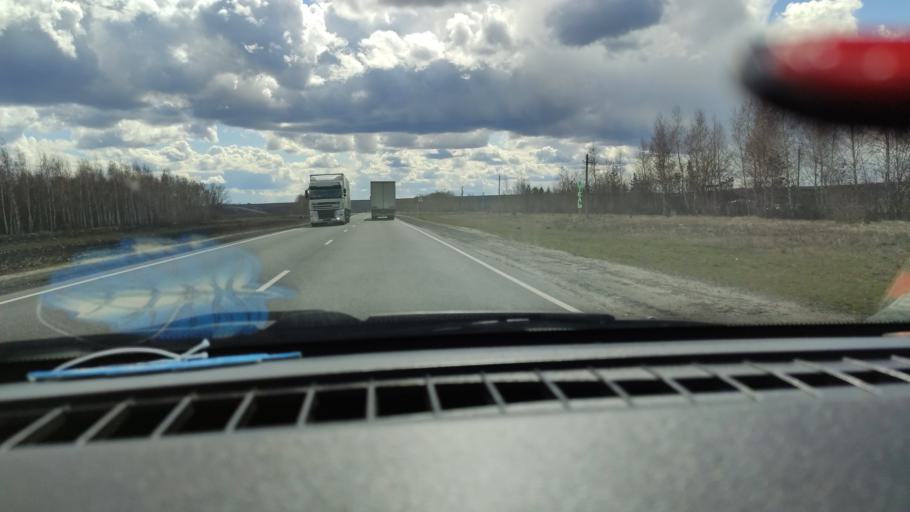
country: RU
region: Samara
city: Syzran'
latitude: 52.9843
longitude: 48.3159
